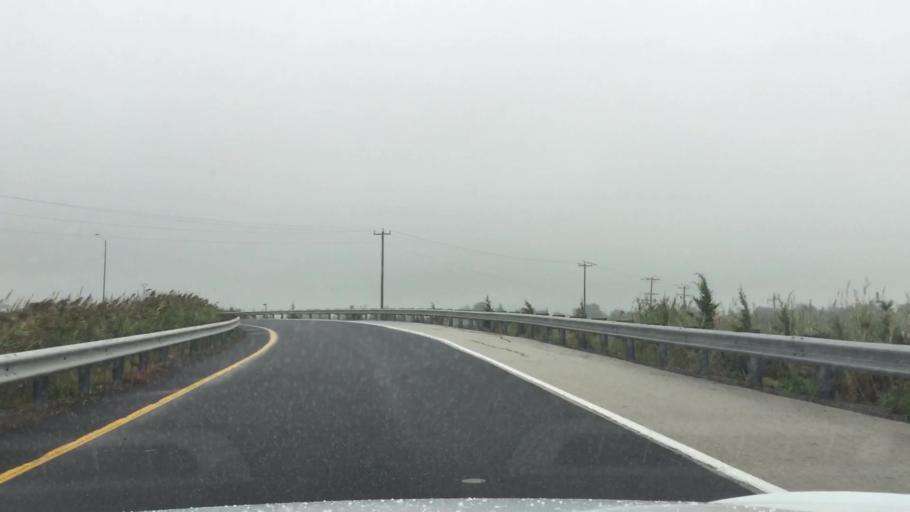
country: CA
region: Ontario
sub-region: Lambton County
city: Walpole Island
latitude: 42.2414
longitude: -82.5539
